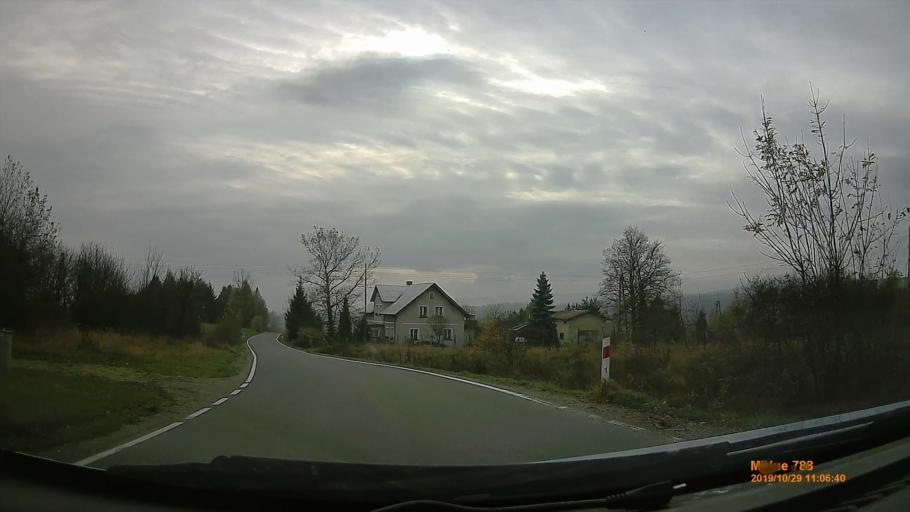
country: PL
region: Lower Silesian Voivodeship
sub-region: Powiat klodzki
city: Szczytna
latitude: 50.4623
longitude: 16.4812
